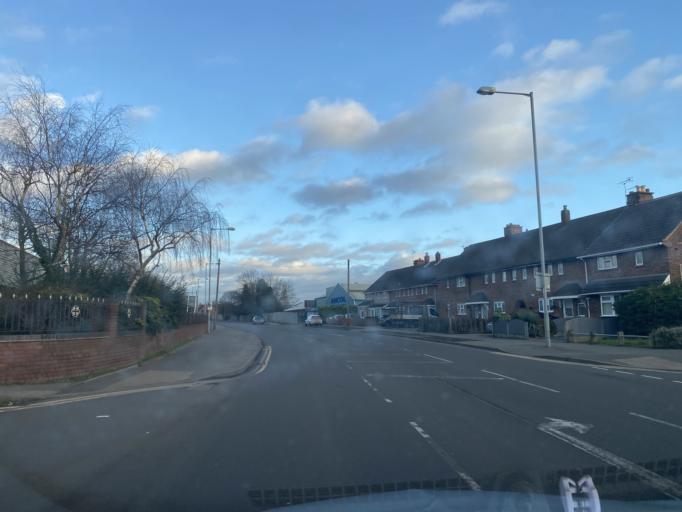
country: GB
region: England
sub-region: Walsall
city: Bloxwich
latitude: 52.6055
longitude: -2.0113
